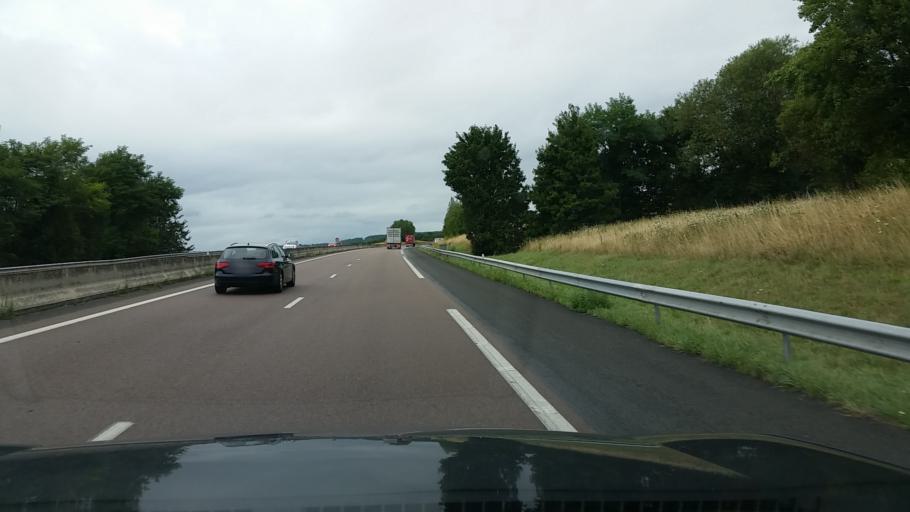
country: FR
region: Lorraine
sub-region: Departement des Vosges
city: Chatenois
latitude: 48.3344
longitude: 5.8549
